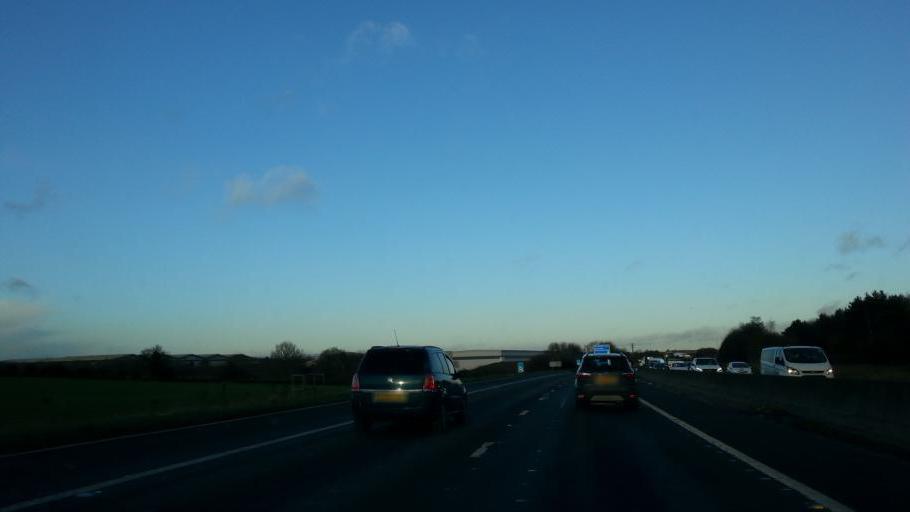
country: GB
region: England
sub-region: Warwickshire
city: Kingsbury
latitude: 52.5962
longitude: -1.6509
